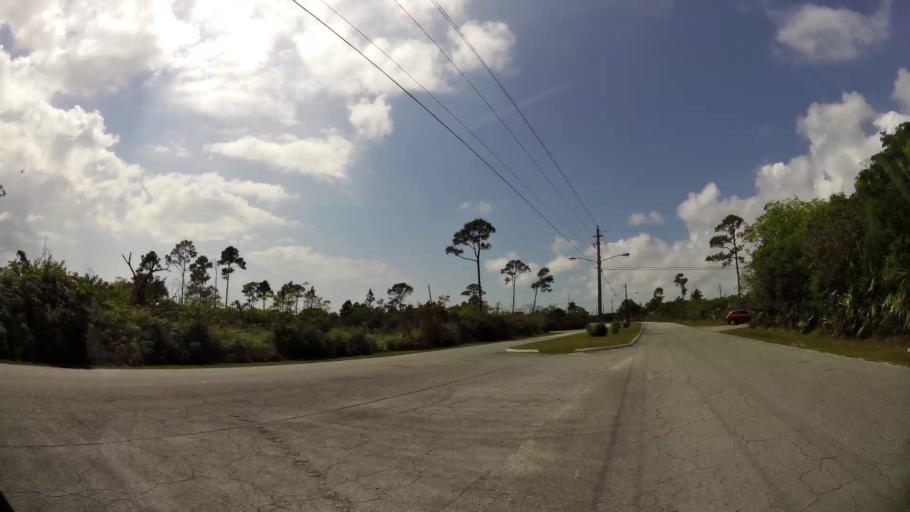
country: BS
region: Freeport
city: Freeport
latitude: 26.5022
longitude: -78.7015
